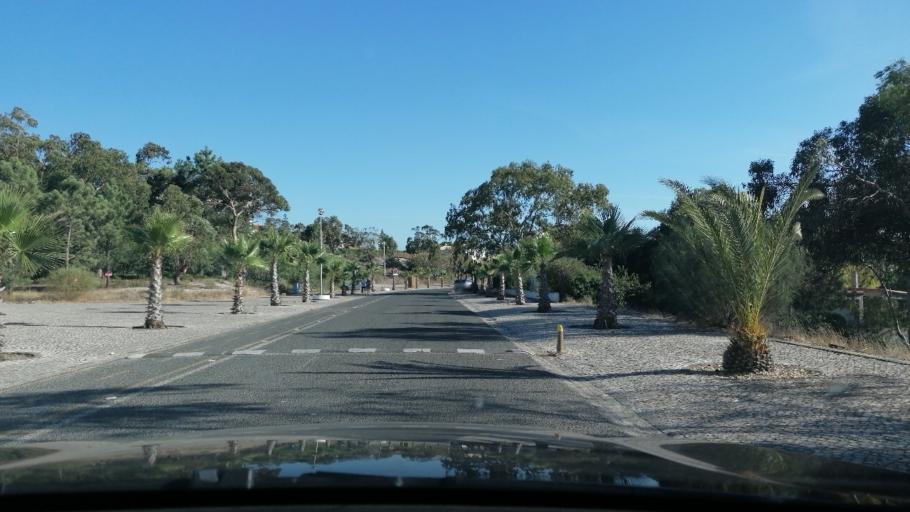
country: PT
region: Setubal
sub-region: Setubal
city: Setubal
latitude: 38.4558
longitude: -8.8579
